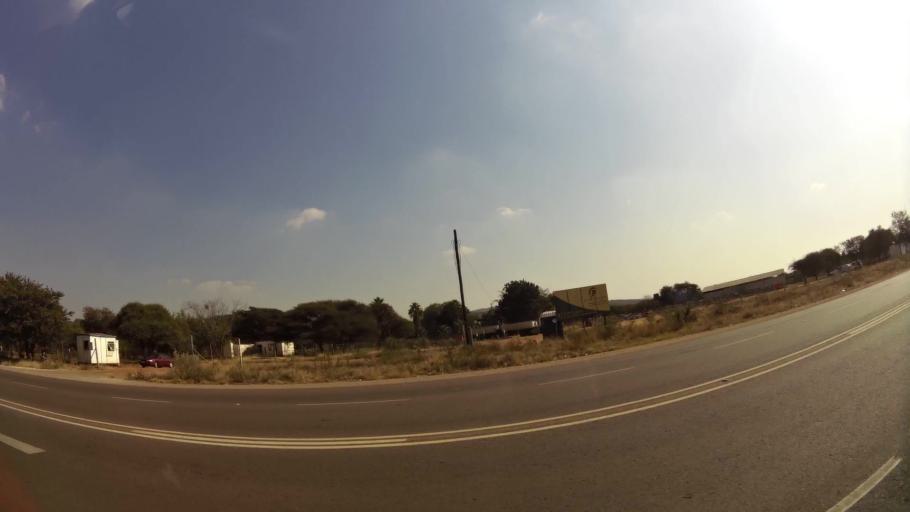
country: ZA
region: North-West
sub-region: Bojanala Platinum District Municipality
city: Mogwase
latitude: -25.4430
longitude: 27.0880
